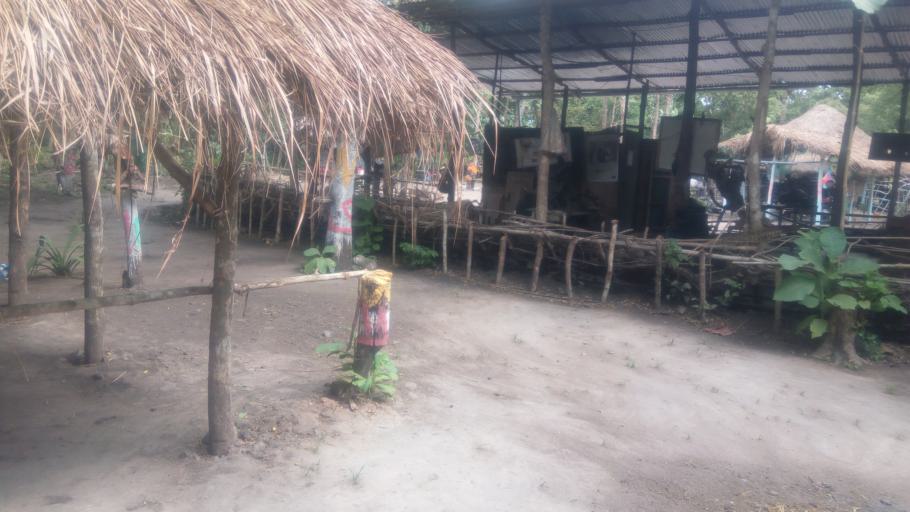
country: TG
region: Maritime
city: Tsevie
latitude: 6.4749
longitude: 1.1891
